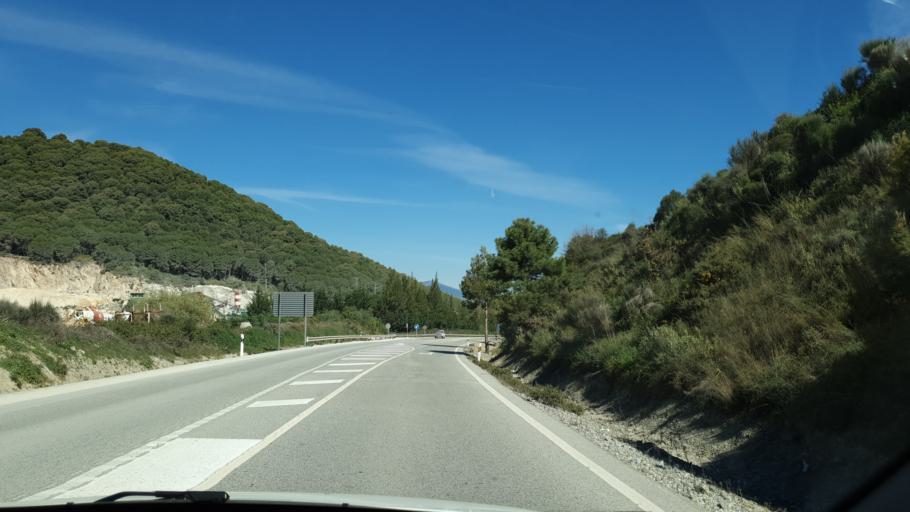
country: ES
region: Andalusia
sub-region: Provincia de Malaga
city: Ojen
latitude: 36.5846
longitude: -4.8527
